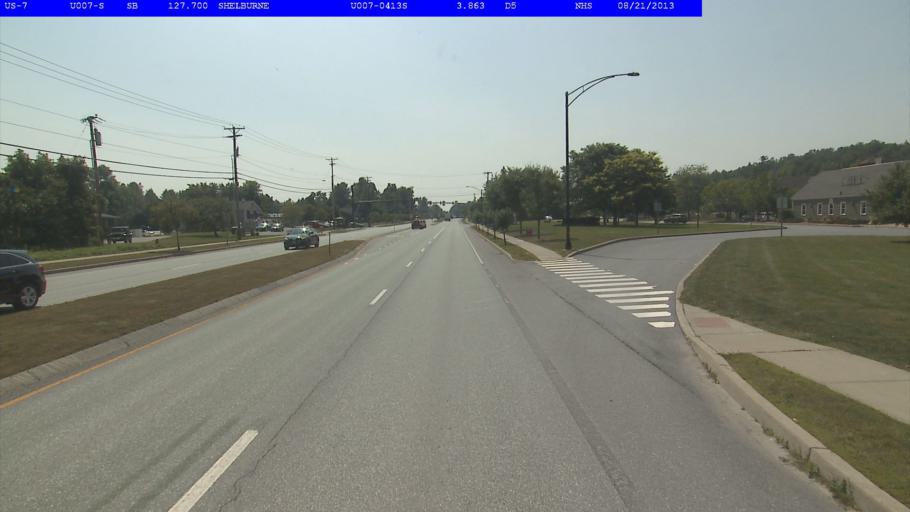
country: US
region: Vermont
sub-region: Chittenden County
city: Burlington
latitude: 44.3975
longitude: -73.2195
